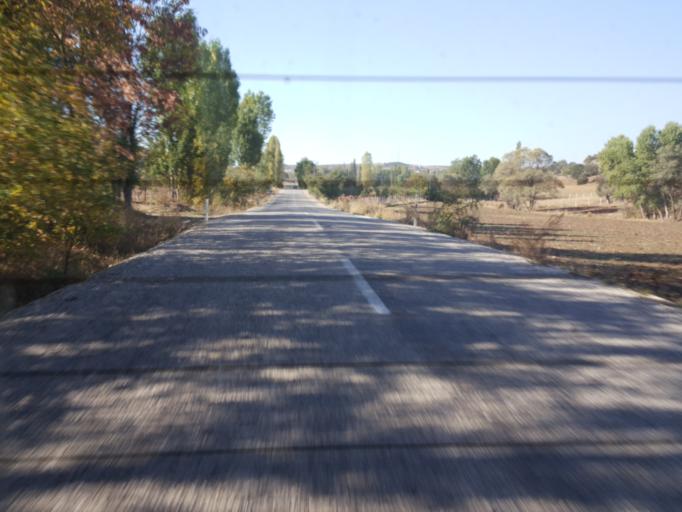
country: TR
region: Corum
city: Seydim
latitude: 40.5552
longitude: 34.7575
